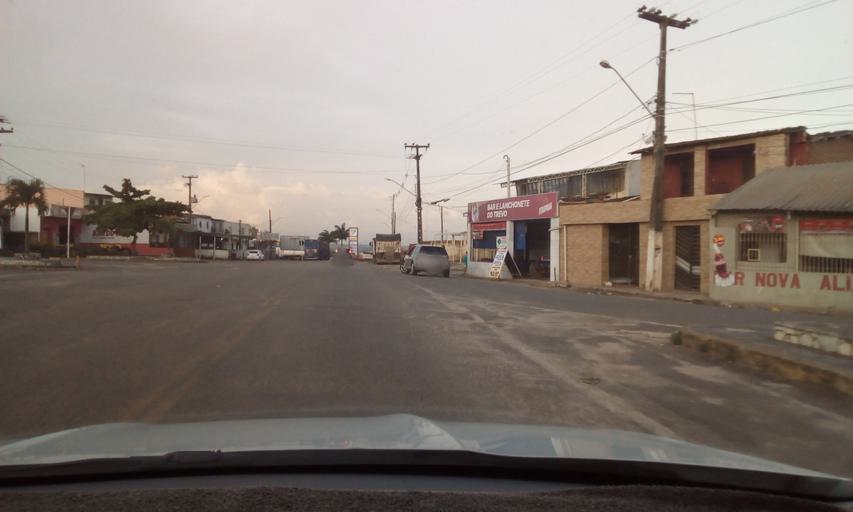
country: BR
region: Pernambuco
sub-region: Vicencia
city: Vicencia
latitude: -7.5976
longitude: -35.2308
